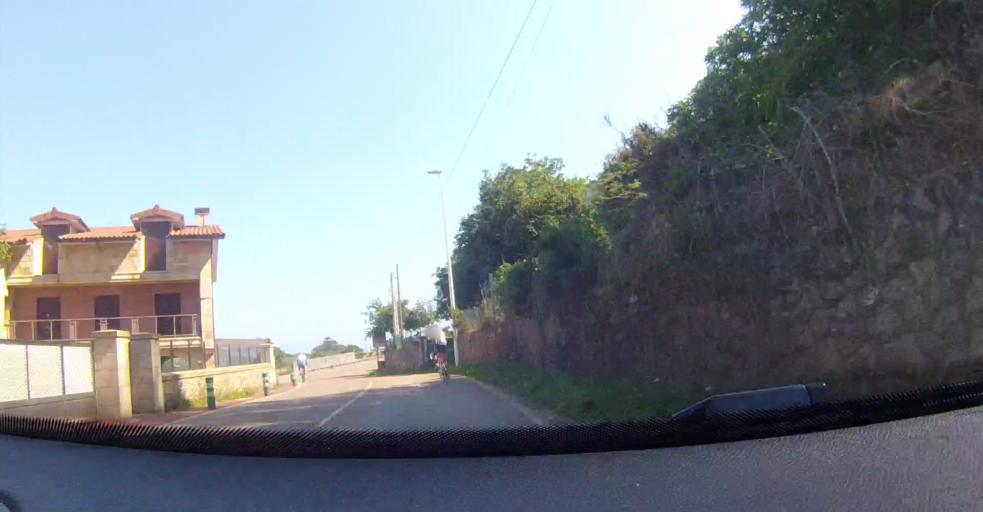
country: ES
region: Cantabria
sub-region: Provincia de Cantabria
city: Noja
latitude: 43.4651
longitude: -3.5195
